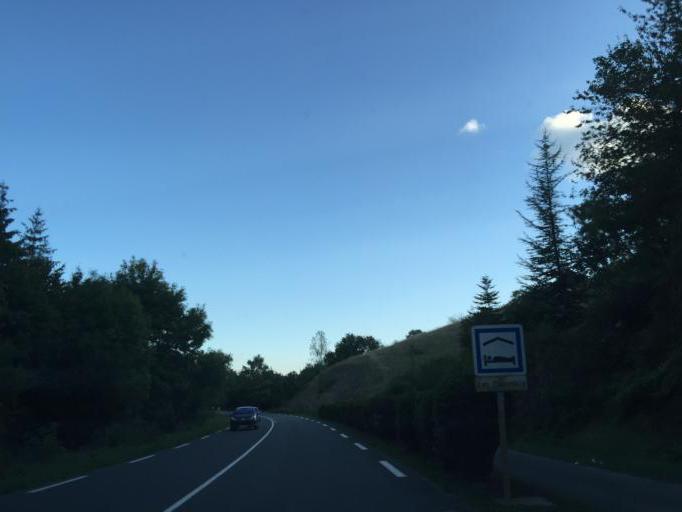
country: FR
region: Midi-Pyrenees
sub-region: Departement de l'Aveyron
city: Rodez
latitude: 44.3886
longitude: 2.5663
